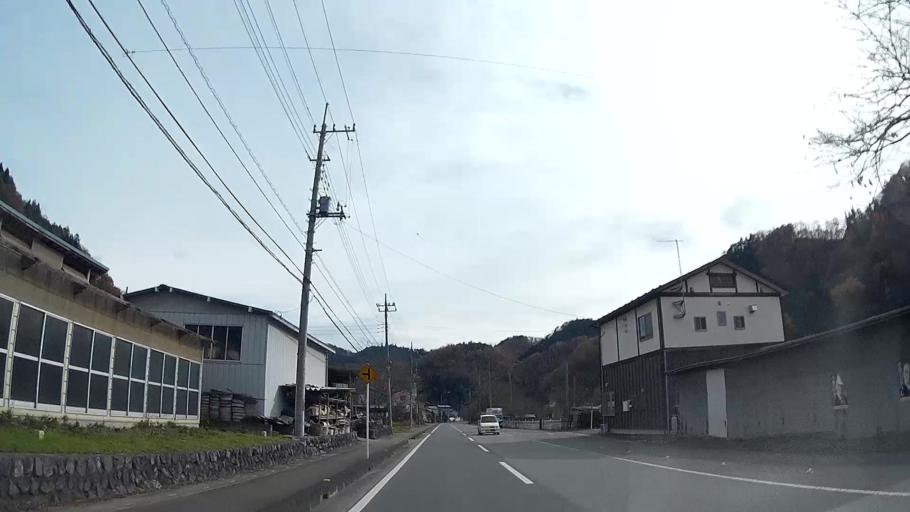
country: JP
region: Saitama
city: Chichibu
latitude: 36.0452
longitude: 138.9931
